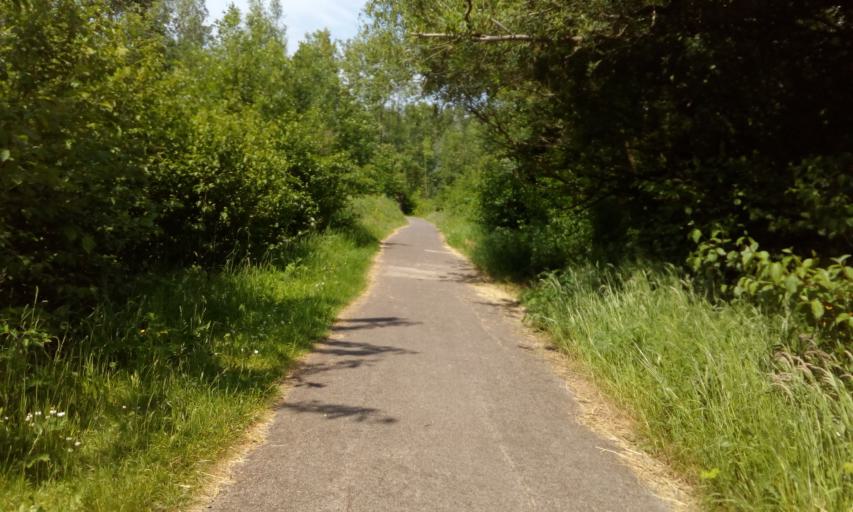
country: NL
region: South Holland
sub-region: Gemeente Pijnacker-Nootdorp
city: Pijnacker
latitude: 52.0458
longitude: 4.4555
